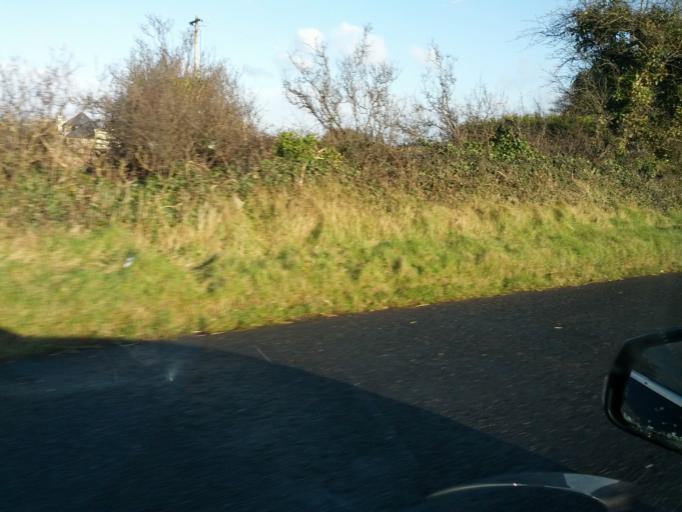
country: IE
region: Connaught
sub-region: County Galway
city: Gort
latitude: 53.1637
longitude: -8.8141
